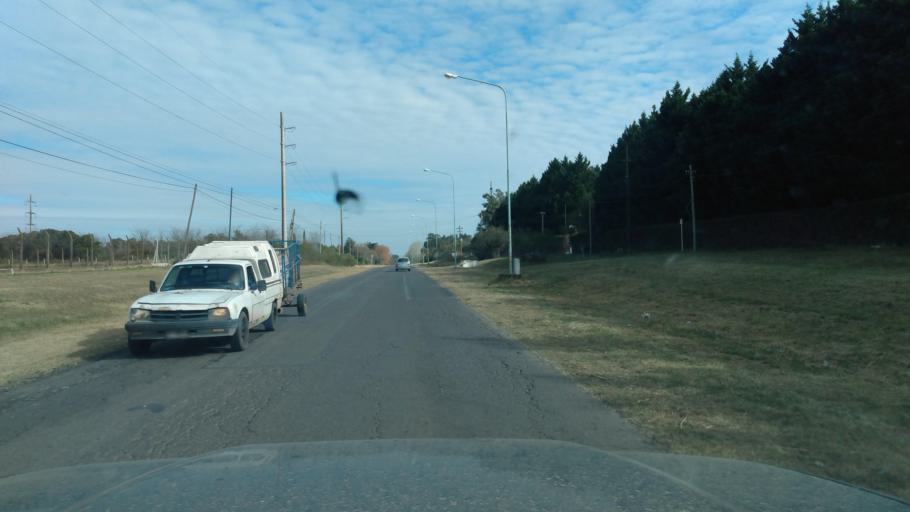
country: AR
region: Buenos Aires
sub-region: Partido de Lujan
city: Lujan
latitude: -34.5696
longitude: -59.1519
